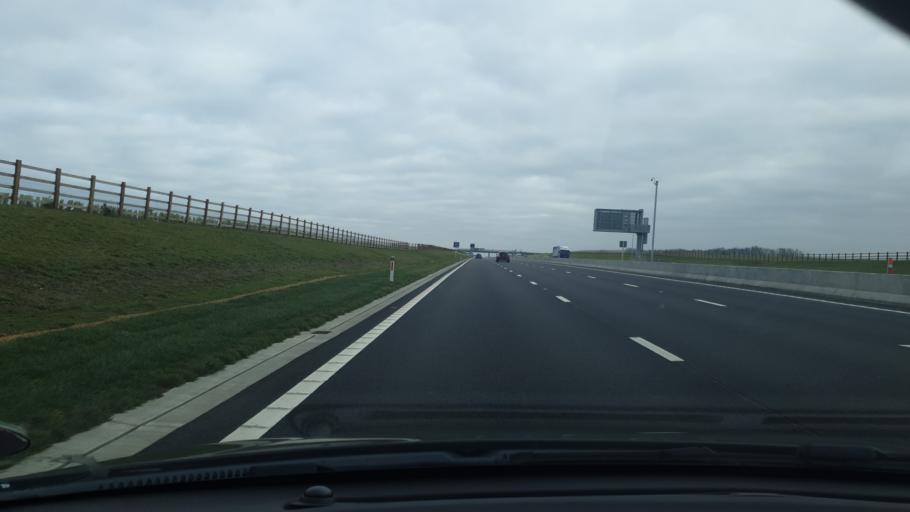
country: GB
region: England
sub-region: Cambridgeshire
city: Godmanchester
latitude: 52.2969
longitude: -0.1834
